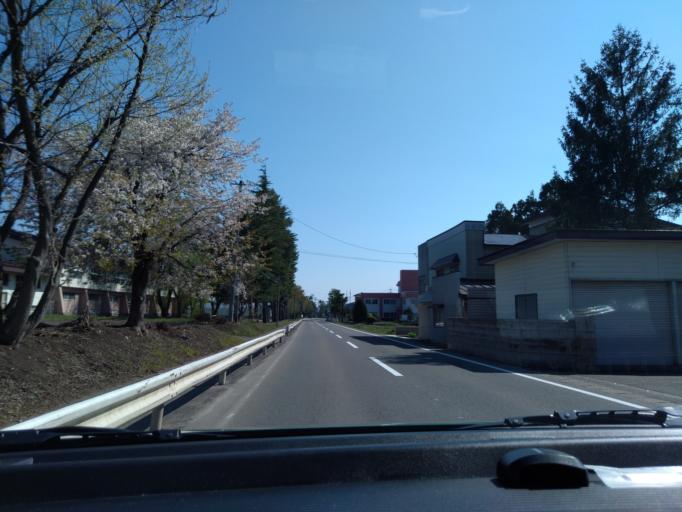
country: JP
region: Akita
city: Omagari
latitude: 39.4659
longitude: 140.5822
